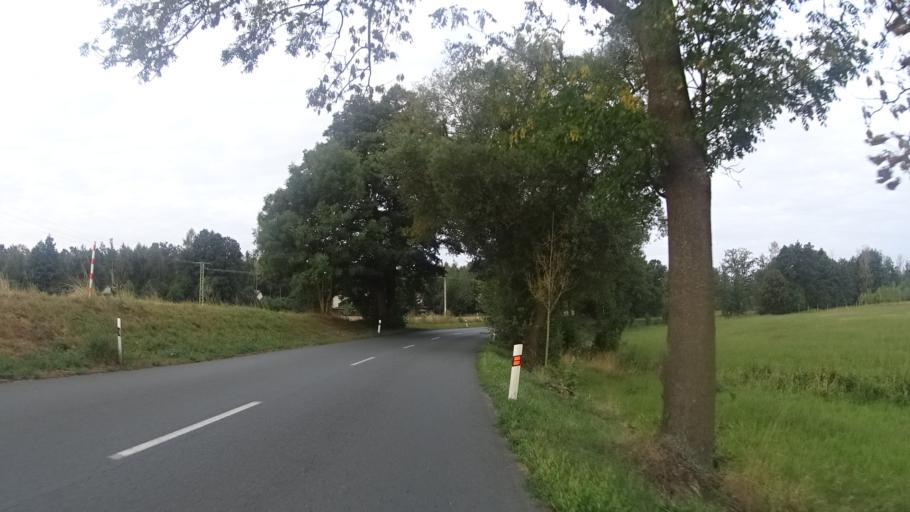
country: CZ
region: Kralovehradecky
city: Cernilov
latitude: 50.2077
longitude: 15.8993
